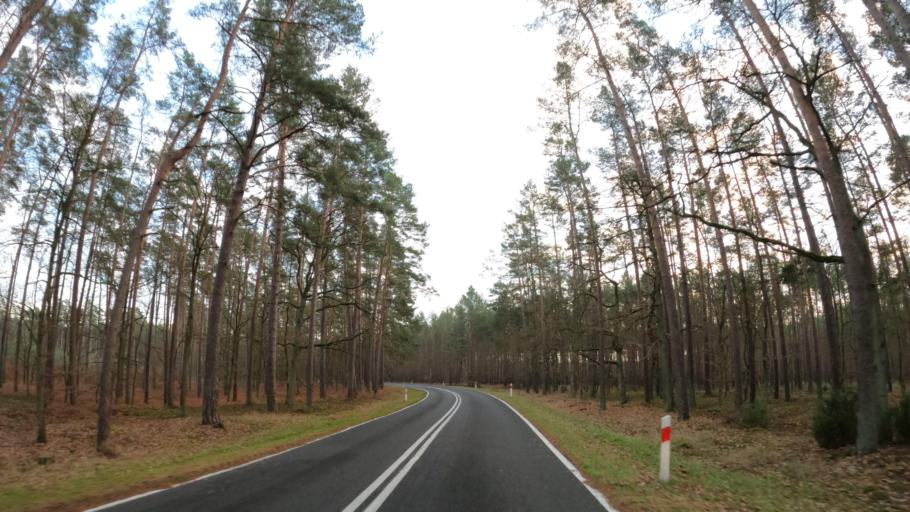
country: PL
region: West Pomeranian Voivodeship
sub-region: Powiat policki
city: Nowe Warpno
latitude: 53.6796
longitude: 14.3589
